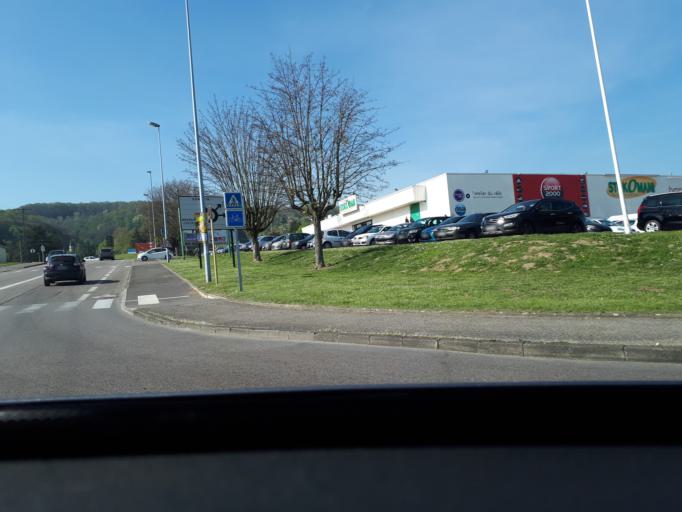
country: FR
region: Rhone-Alpes
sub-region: Departement de l'Isere
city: Domarin
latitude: 45.5904
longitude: 5.2476
